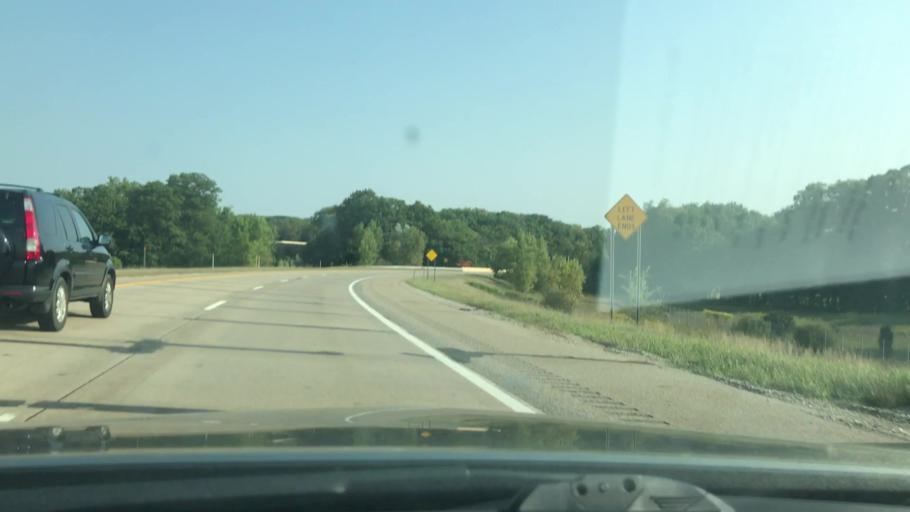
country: US
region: Michigan
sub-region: Kent County
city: Forest Hills
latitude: 42.8841
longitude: -85.4910
